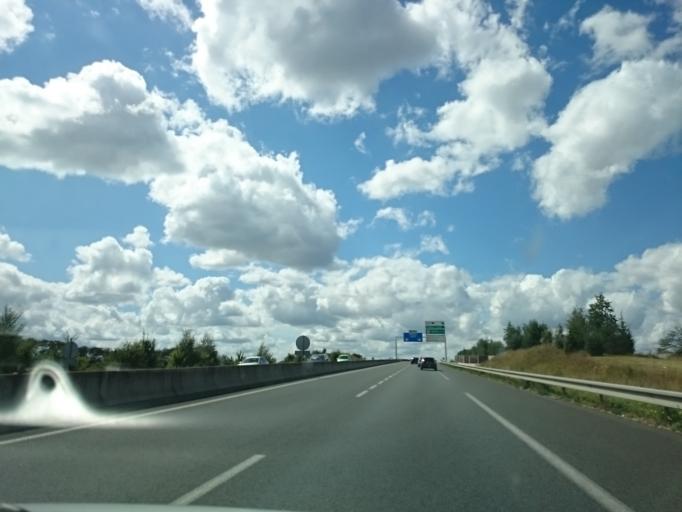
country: FR
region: Pays de la Loire
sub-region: Departement de Maine-et-Loire
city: Beaucouze
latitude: 47.4946
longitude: -0.6154
